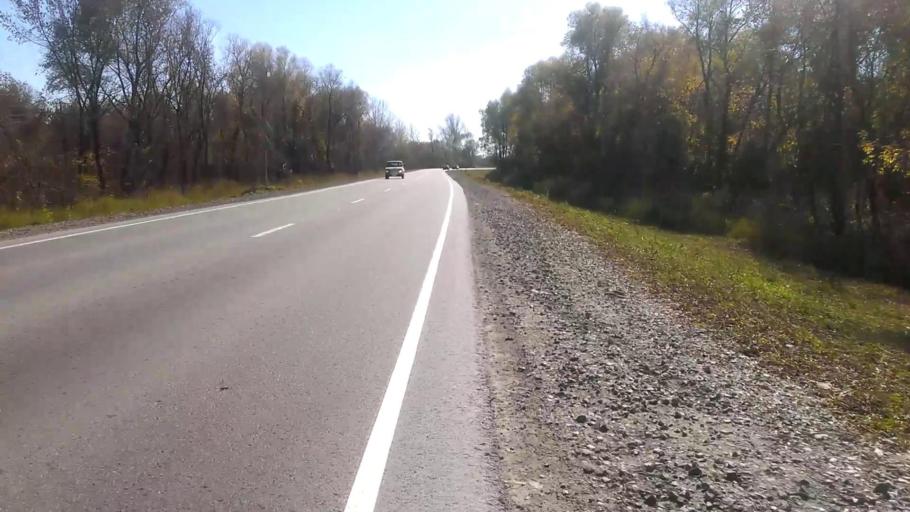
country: RU
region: Altai Krai
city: Sannikovo
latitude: 53.3256
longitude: 83.9421
